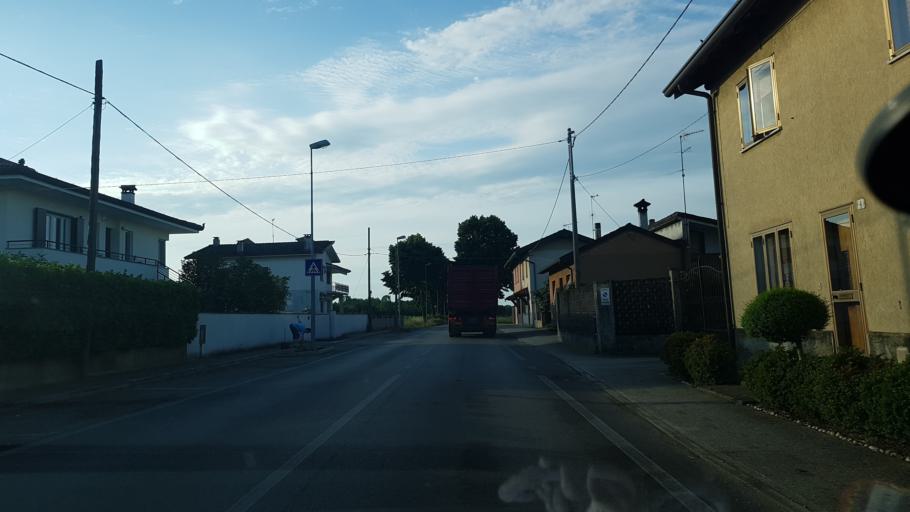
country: IT
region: Friuli Venezia Giulia
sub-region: Provincia di Udine
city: Chiopris
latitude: 45.9215
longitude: 13.4042
